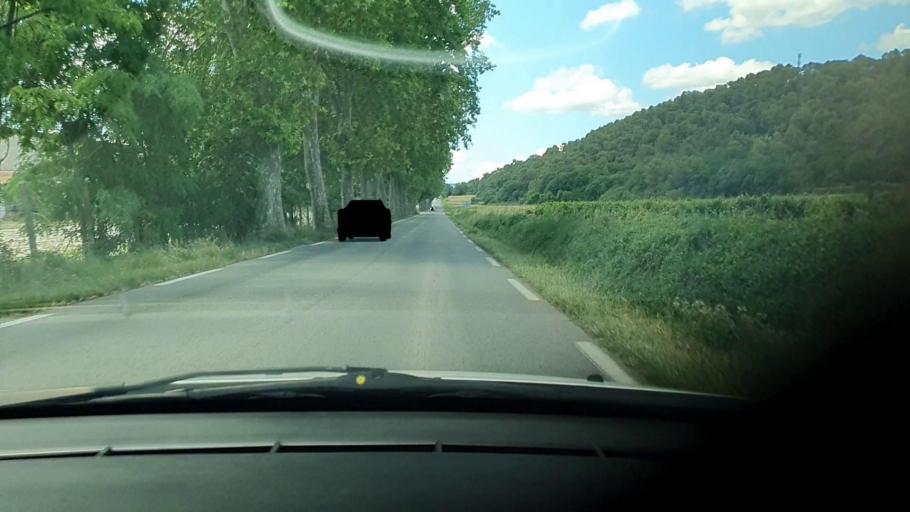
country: FR
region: Languedoc-Roussillon
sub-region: Departement du Gard
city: Montaren-et-Saint-Mediers
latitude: 44.0312
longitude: 4.3724
